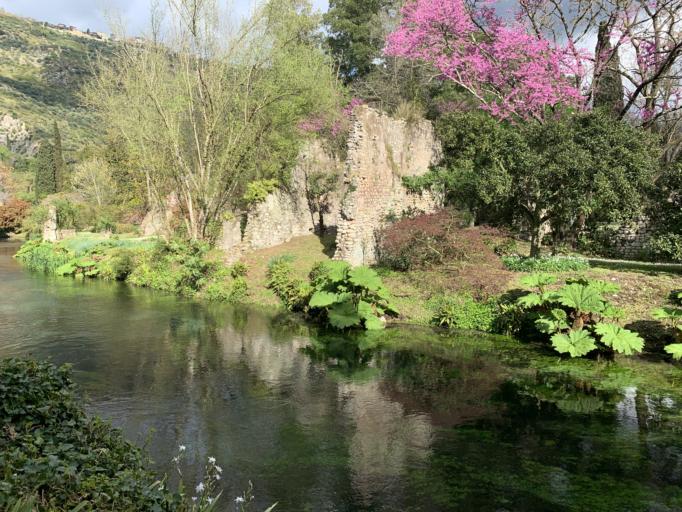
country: IT
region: Latium
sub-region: Provincia di Latina
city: Norma
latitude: 41.5812
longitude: 12.9545
